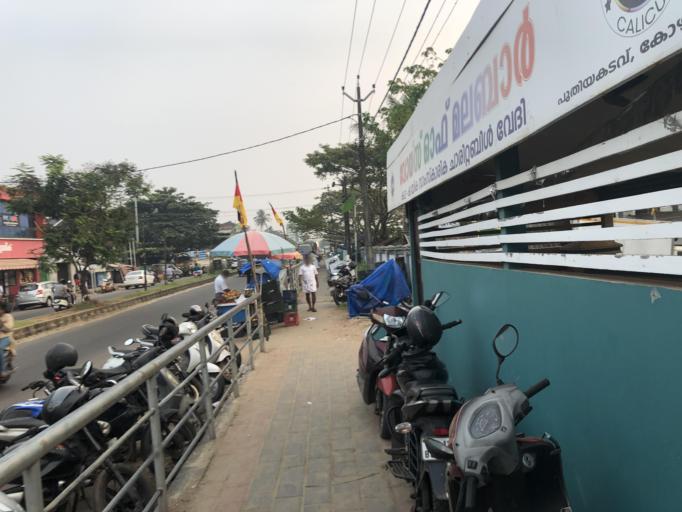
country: IN
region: Kerala
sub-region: Kozhikode
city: Kozhikode
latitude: 11.2662
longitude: 75.7669
